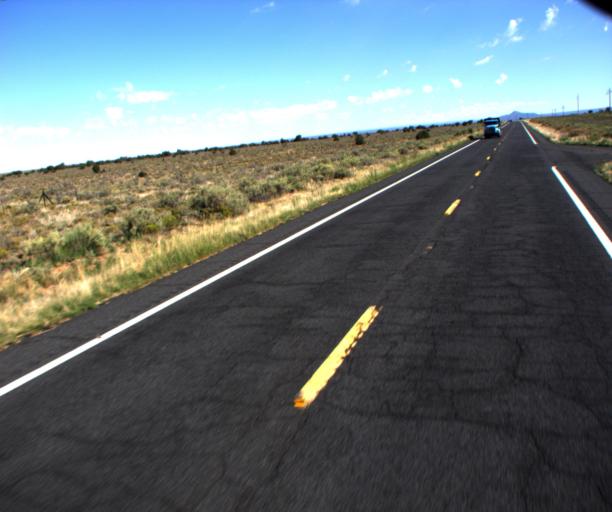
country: US
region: Arizona
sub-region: Coconino County
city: Williams
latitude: 35.5968
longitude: -112.1481
